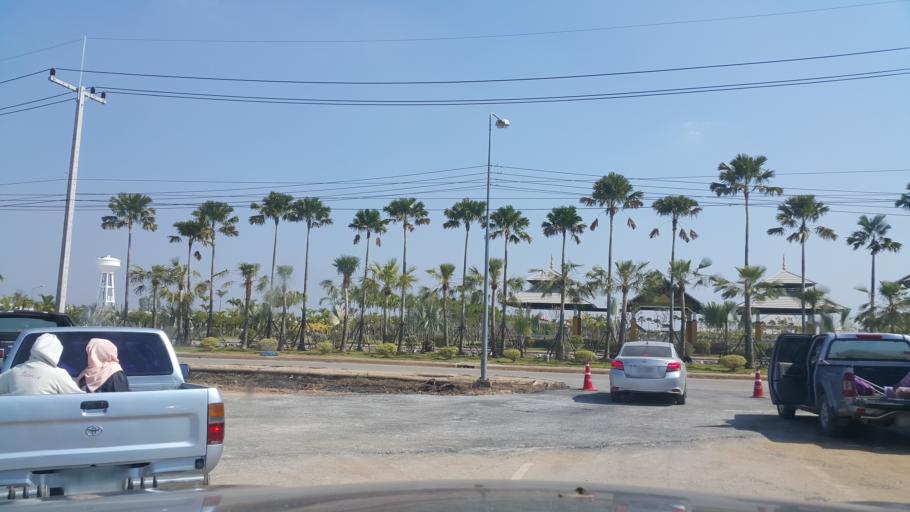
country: TH
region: Khon Kaen
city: Khon Kaen
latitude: 16.5130
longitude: 102.8687
